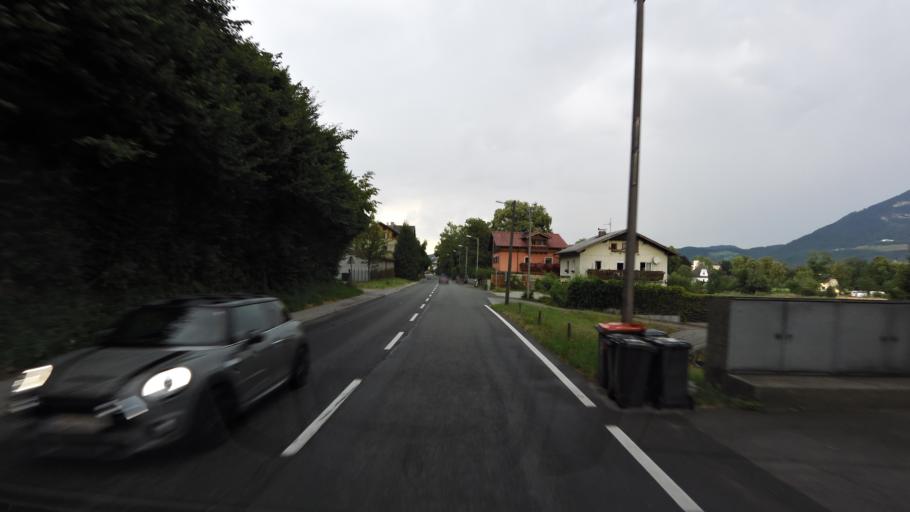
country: AT
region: Salzburg
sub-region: Politischer Bezirk Salzburg-Umgebung
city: Anif
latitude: 47.7675
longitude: 13.0589
